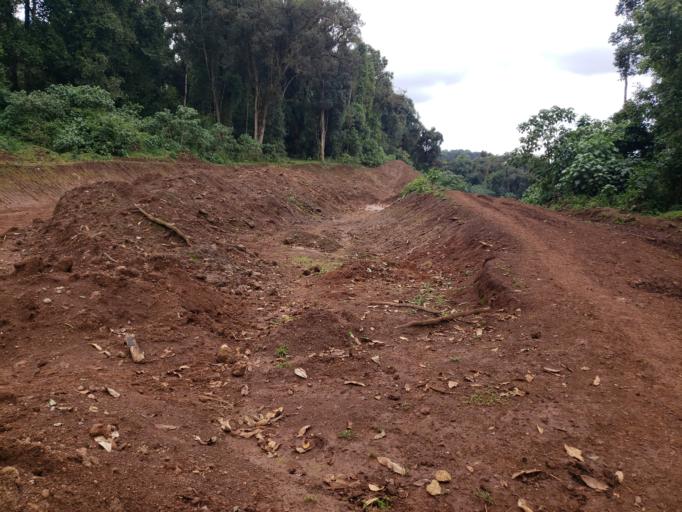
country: ET
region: Oromiya
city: Dodola
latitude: 6.5851
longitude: 39.4150
